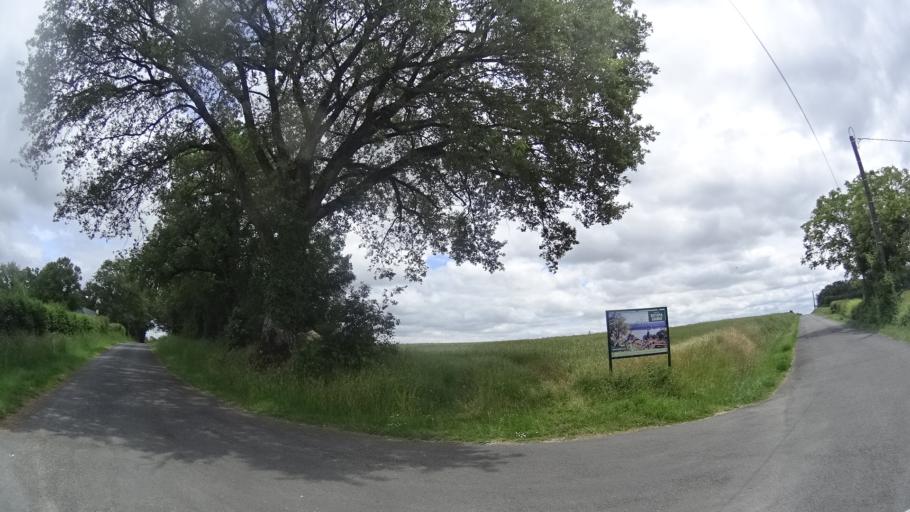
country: FR
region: Pays de la Loire
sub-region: Departement de Maine-et-Loire
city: Chenehutte-Treves-Cunault
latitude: 47.2905
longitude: -0.1466
